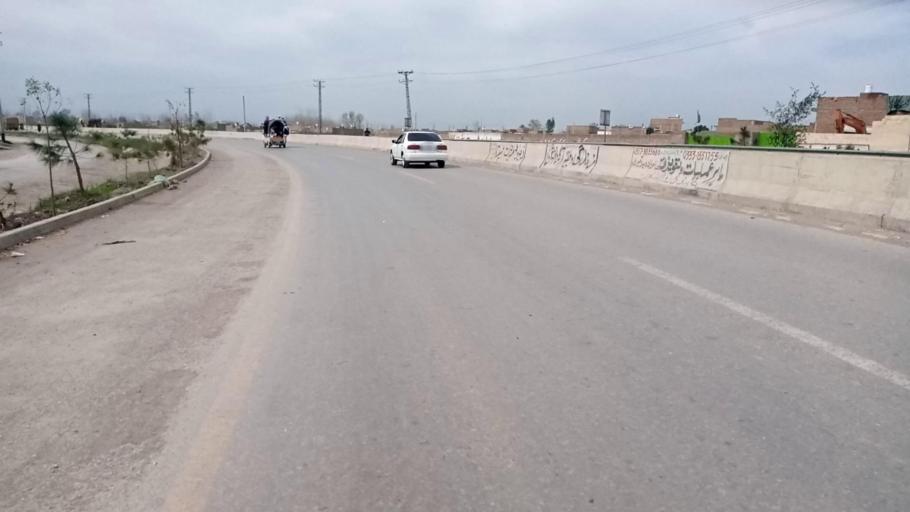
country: PK
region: Khyber Pakhtunkhwa
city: Peshawar
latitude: 34.0343
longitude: 71.6417
